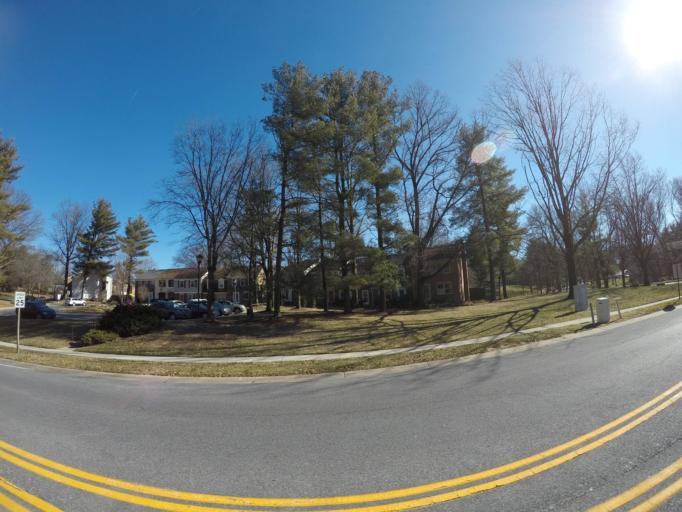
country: US
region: Maryland
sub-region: Howard County
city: Columbia
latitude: 39.2130
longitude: -76.8172
